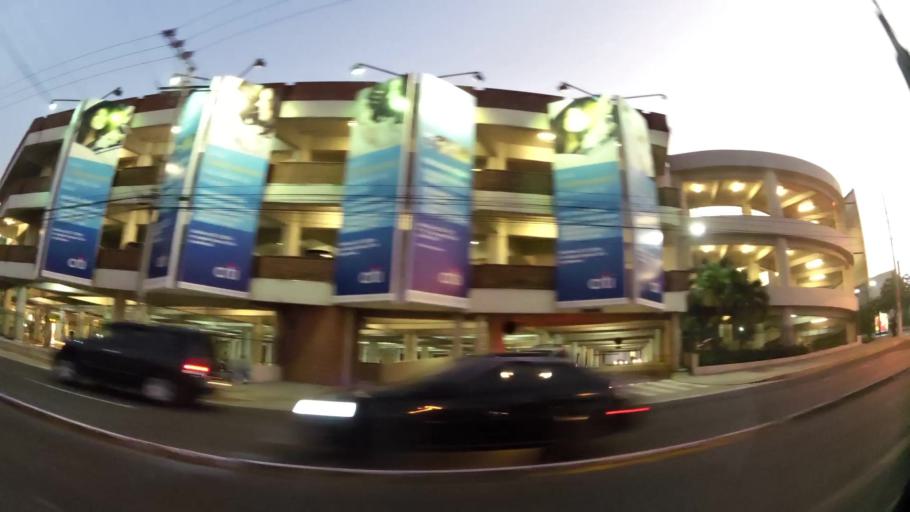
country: SV
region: La Libertad
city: Antiguo Cuscatlan
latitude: 13.6785
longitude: -89.2550
